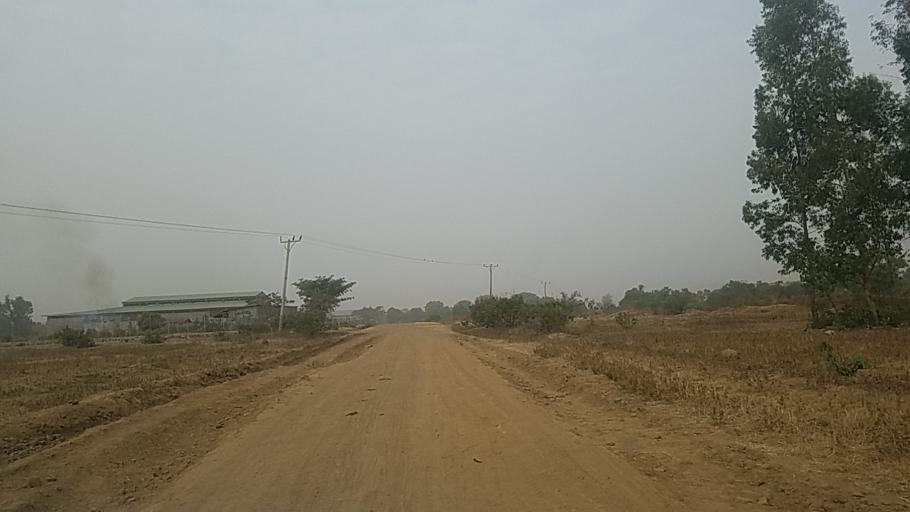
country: ET
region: Amhara
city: Bure
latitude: 10.9777
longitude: 36.4976
